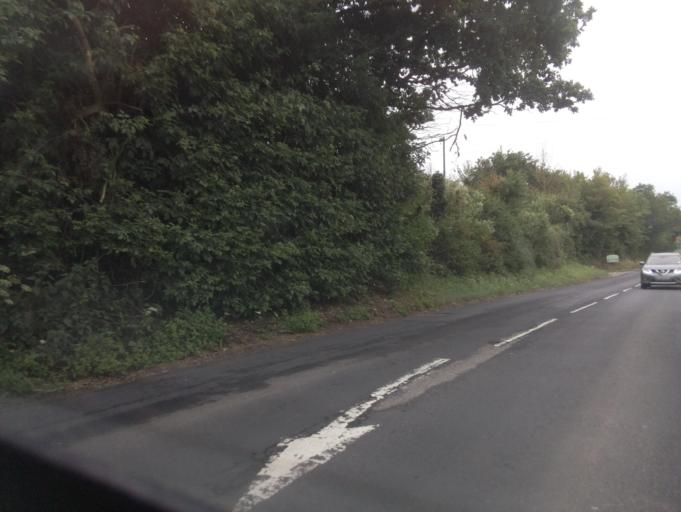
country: GB
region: England
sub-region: Devon
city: Topsham
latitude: 50.7355
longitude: -3.4333
